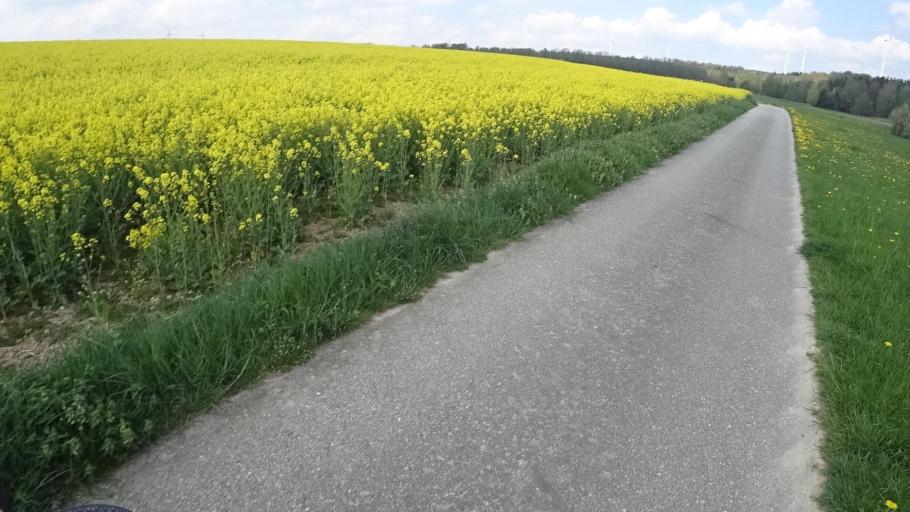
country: DE
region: Rheinland-Pfalz
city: Kisselbach
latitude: 50.0545
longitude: 7.6016
